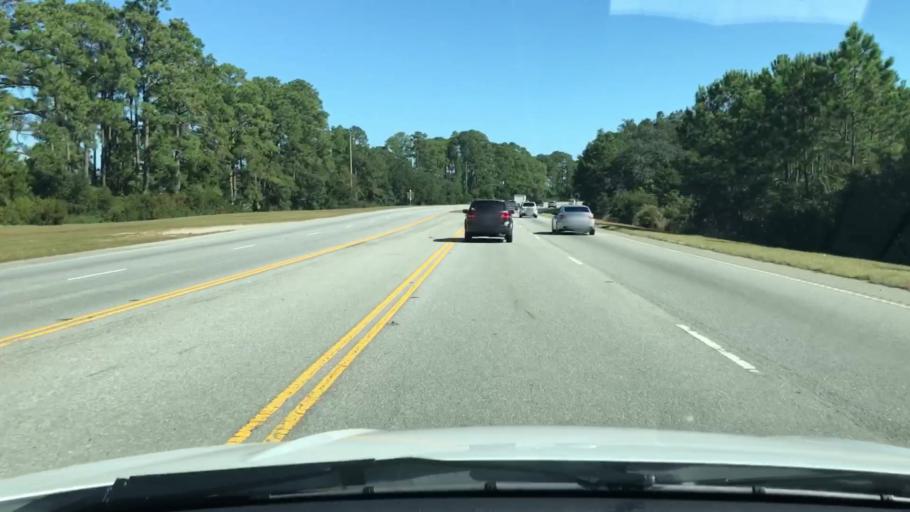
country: US
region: South Carolina
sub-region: Beaufort County
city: Laurel Bay
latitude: 32.3747
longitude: -80.8294
